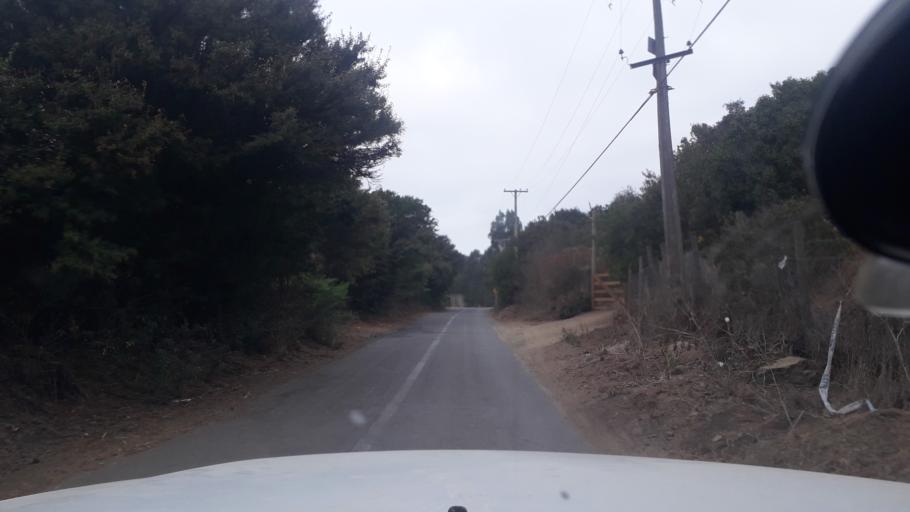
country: CL
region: Valparaiso
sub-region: Provincia de Valparaiso
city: Valparaiso
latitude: -33.1108
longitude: -71.6593
